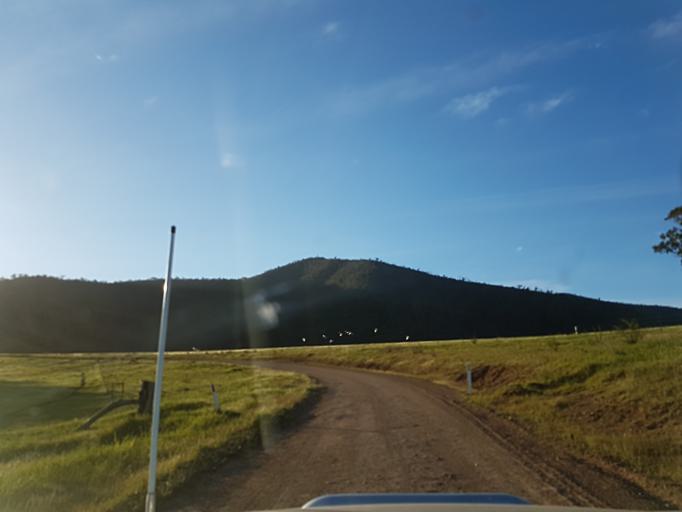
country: AU
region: Victoria
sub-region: East Gippsland
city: Bairnsdale
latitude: -37.4003
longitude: 147.1032
